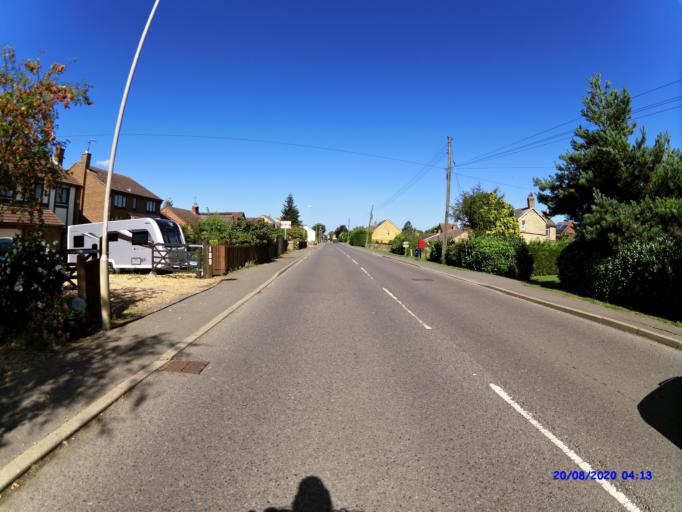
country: GB
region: England
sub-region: Cambridgeshire
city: Ramsey
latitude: 52.4838
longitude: -0.1071
